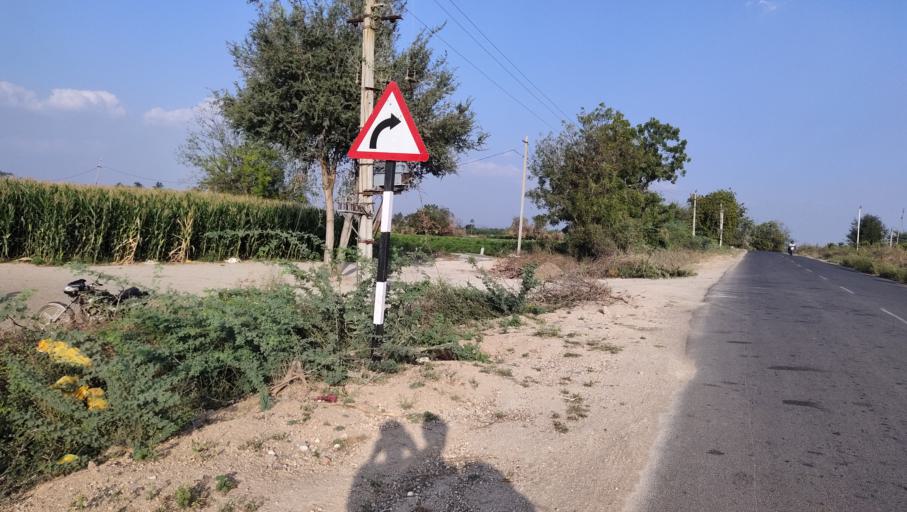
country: IN
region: Andhra Pradesh
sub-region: Anantapur
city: Tadpatri
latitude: 14.9506
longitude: 77.8897
